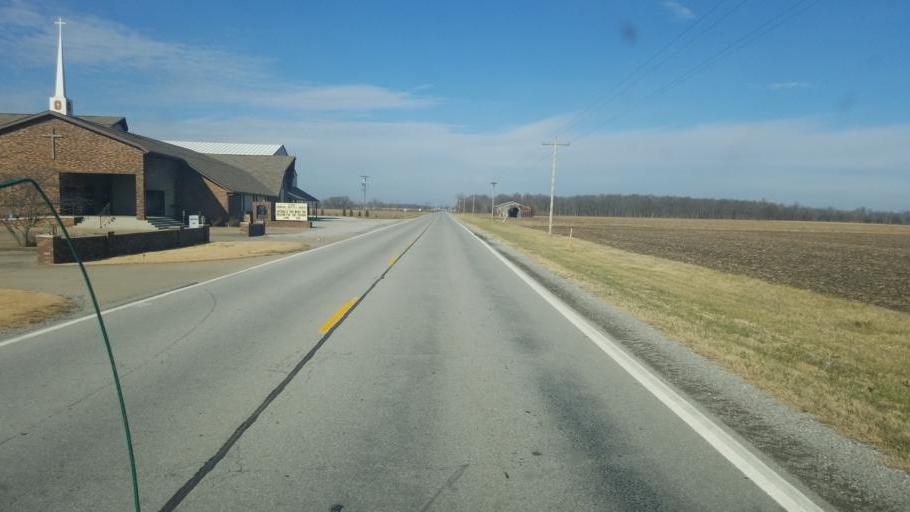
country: US
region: Illinois
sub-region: Saline County
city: Eldorado
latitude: 37.8733
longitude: -88.4529
